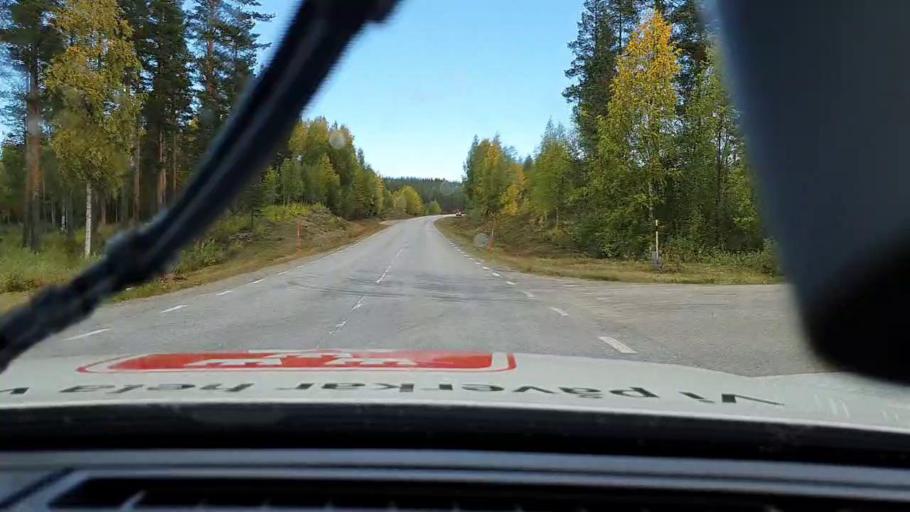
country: SE
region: Vaesterbotten
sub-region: Norsjo Kommun
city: Norsjoe
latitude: 64.9708
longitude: 19.7163
